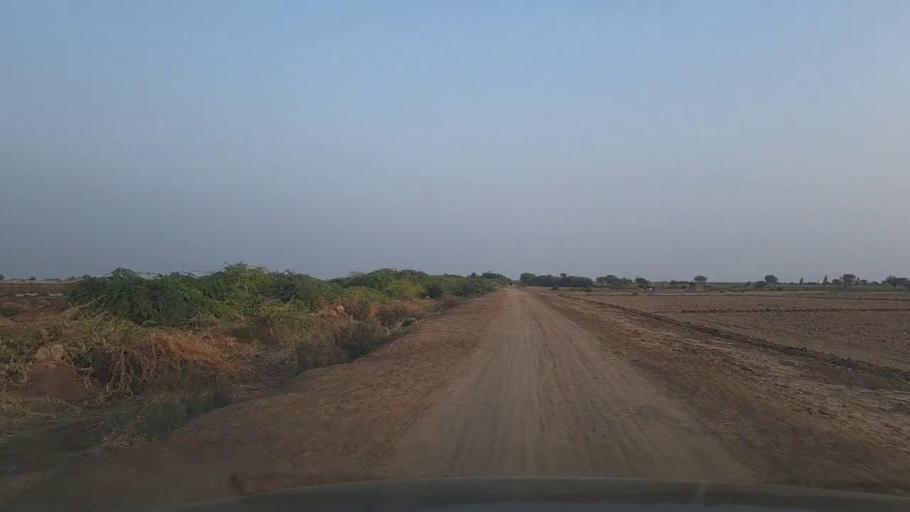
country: PK
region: Sindh
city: Jati
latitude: 24.5403
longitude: 68.4006
